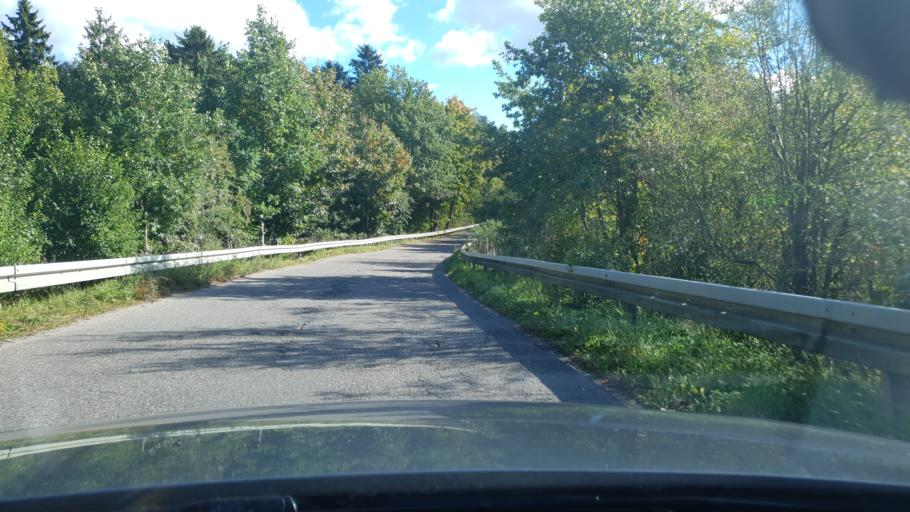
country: PL
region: Pomeranian Voivodeship
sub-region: Powiat pucki
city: Zelistrzewo
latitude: 54.6895
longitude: 18.4245
